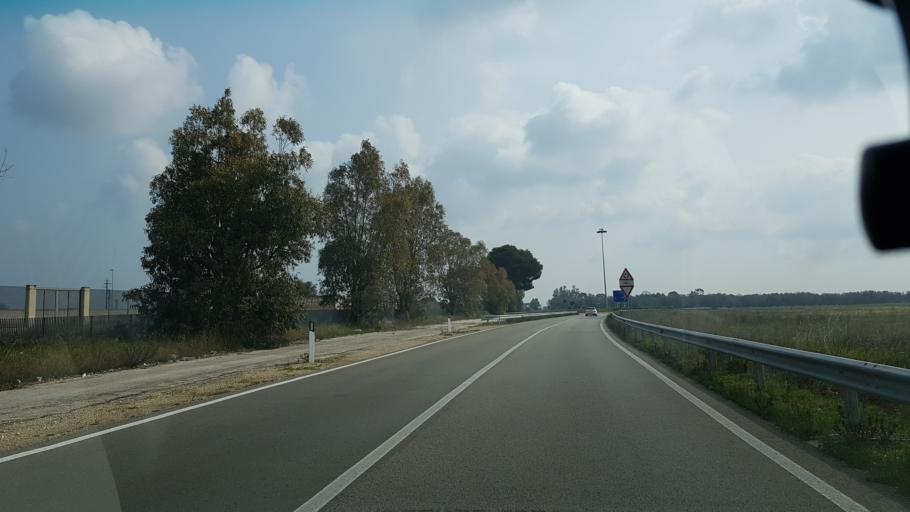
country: IT
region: Apulia
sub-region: Provincia di Brindisi
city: San Pietro Vernotico
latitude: 40.4874
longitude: 18.0177
